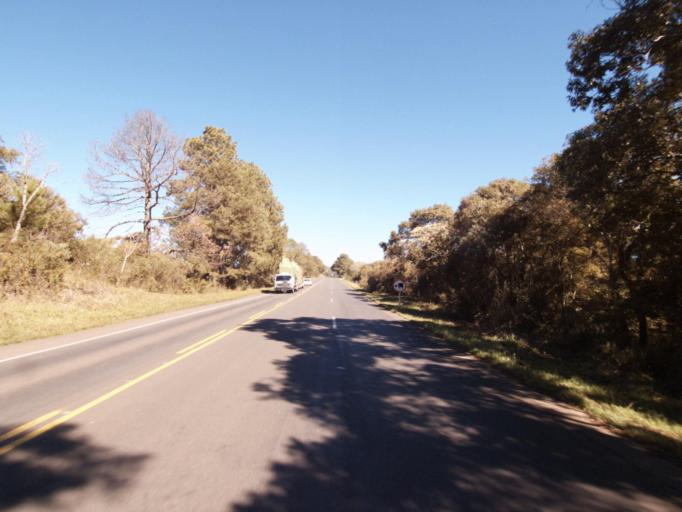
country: BR
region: Santa Catarina
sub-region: Joacaba
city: Joacaba
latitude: -26.9777
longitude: -51.7826
